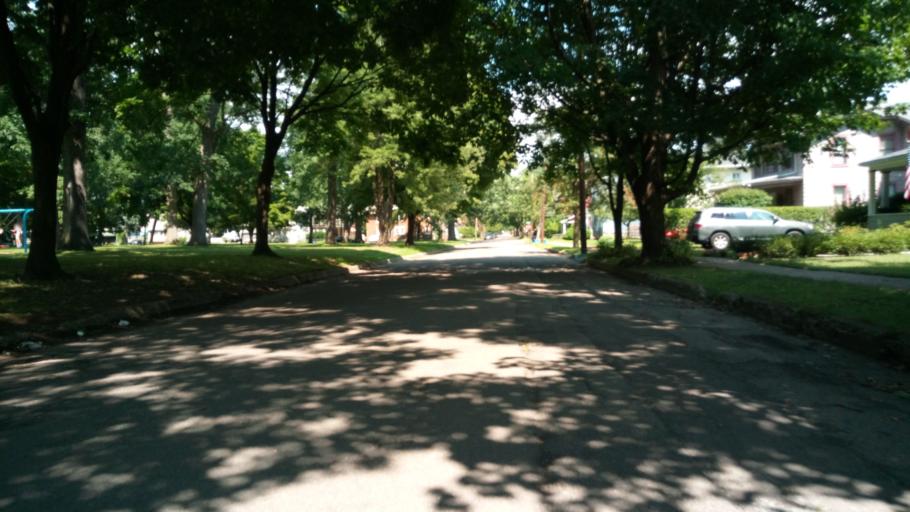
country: US
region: New York
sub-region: Chemung County
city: Elmira
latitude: 42.0916
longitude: -76.8218
